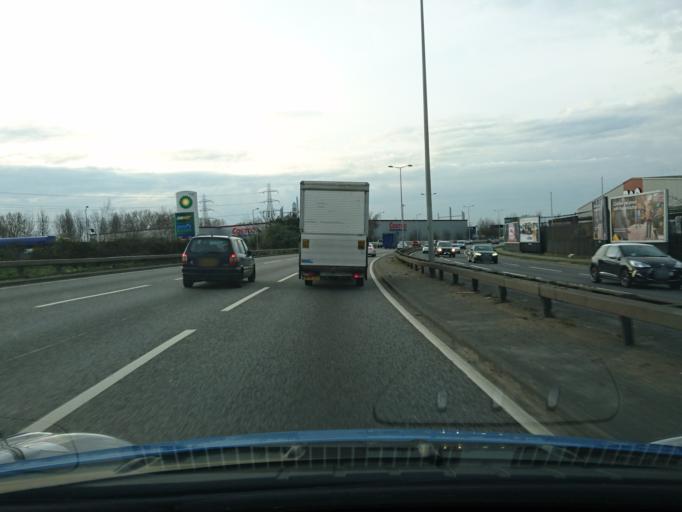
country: GB
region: England
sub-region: Greater London
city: Walthamstow
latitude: 51.6077
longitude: -0.0293
